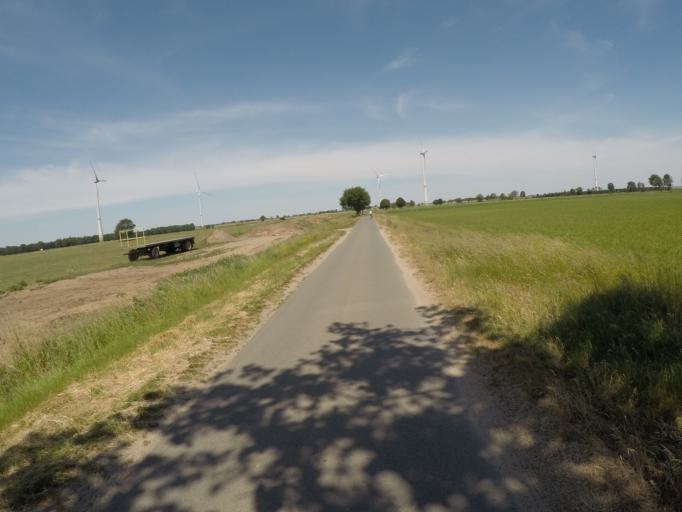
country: BE
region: Flanders
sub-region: Provincie Antwerpen
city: Brecht
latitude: 51.3692
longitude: 4.6669
